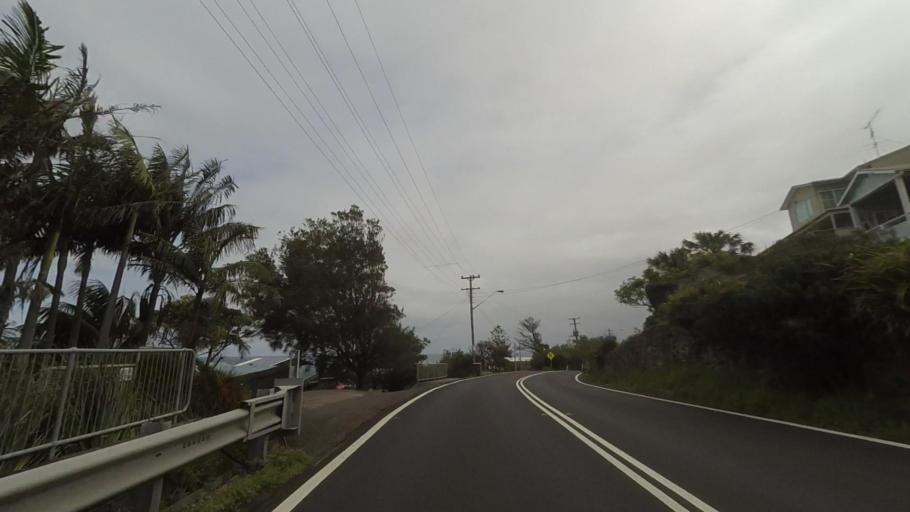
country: AU
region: New South Wales
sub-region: Wollongong
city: Bulli
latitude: -34.2825
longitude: 150.9526
